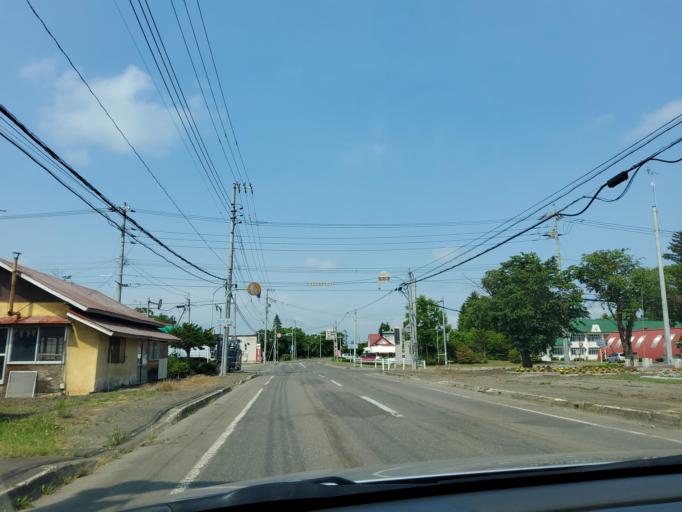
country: JP
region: Hokkaido
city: Obihiro
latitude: 42.8649
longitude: 143.0151
